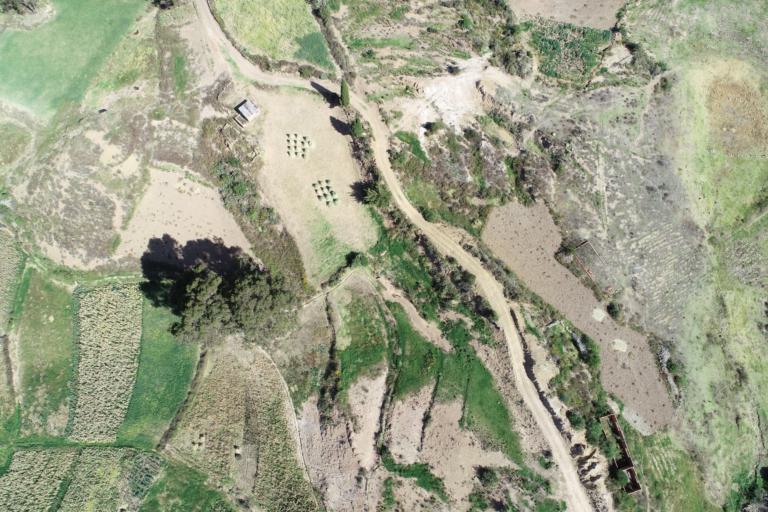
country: BO
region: La Paz
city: La Paz
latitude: -16.5553
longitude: -67.9874
